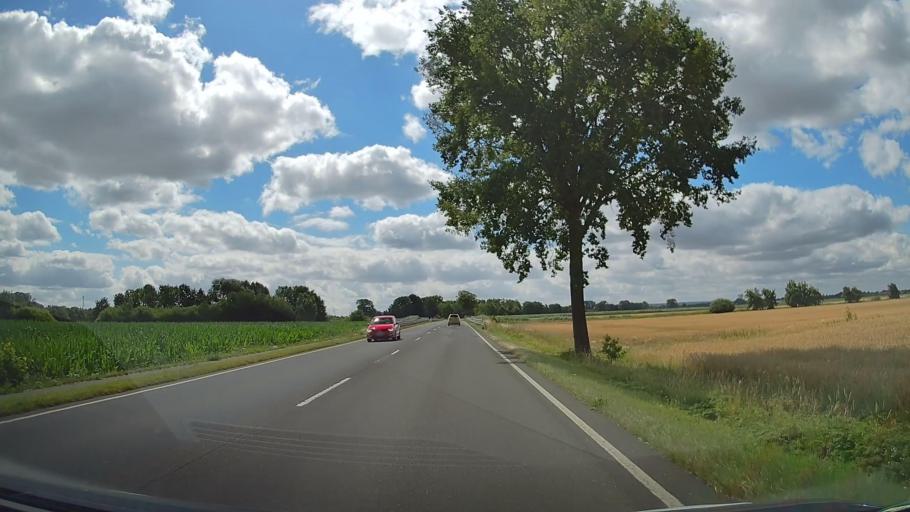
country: DE
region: Lower Saxony
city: Lembruch
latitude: 52.5476
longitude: 8.3713
